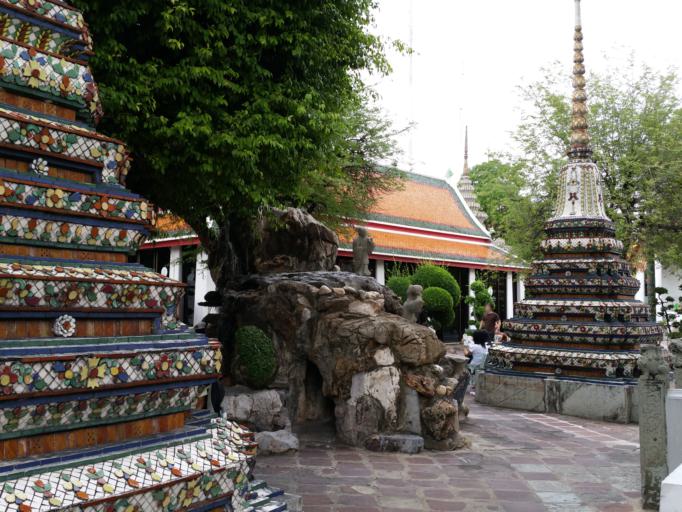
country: TH
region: Bangkok
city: Bangkok
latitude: 13.7468
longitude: 100.4939
